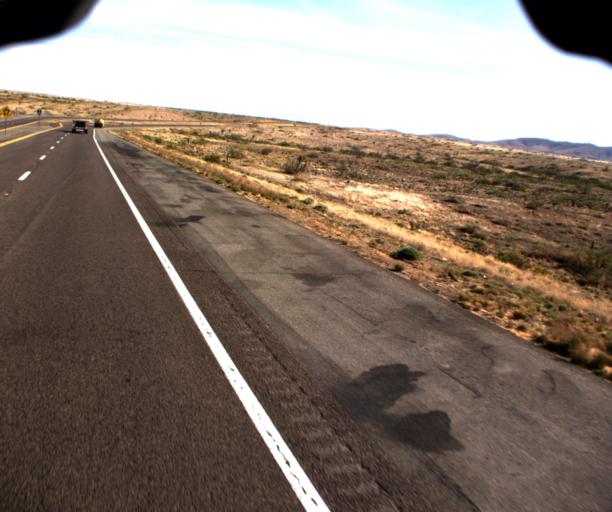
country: US
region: Arizona
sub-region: Cochise County
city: Willcox
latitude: 32.3604
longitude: -109.6814
